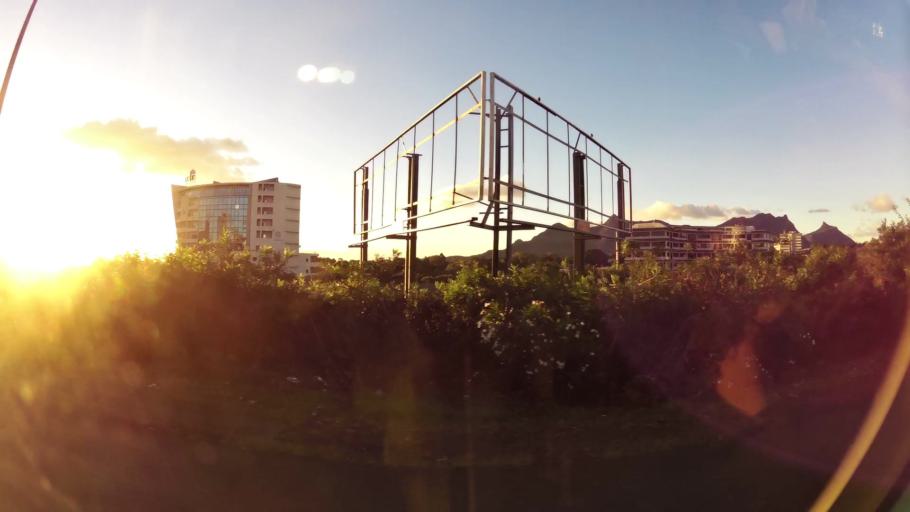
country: MU
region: Plaines Wilhems
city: Ebene
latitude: -20.2419
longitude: 57.4933
